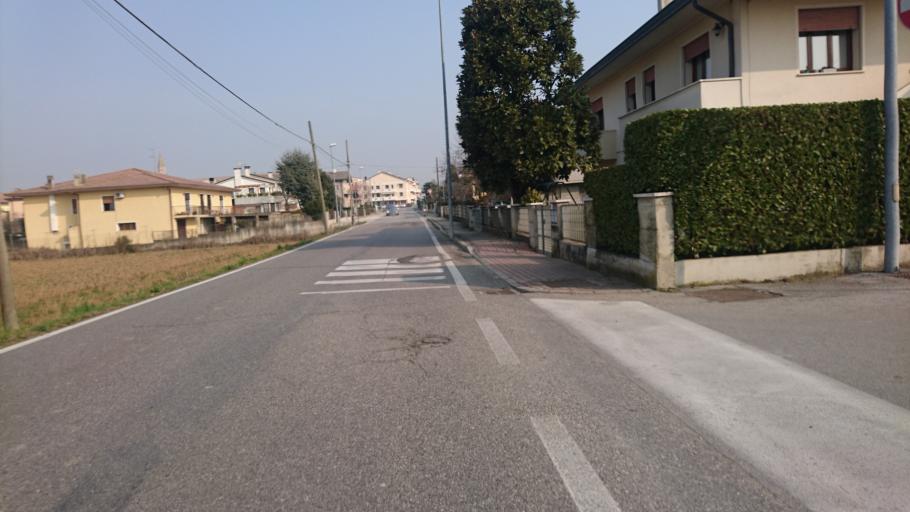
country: IT
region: Veneto
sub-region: Provincia di Padova
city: Veggiano
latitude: 45.4443
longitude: 11.7161
